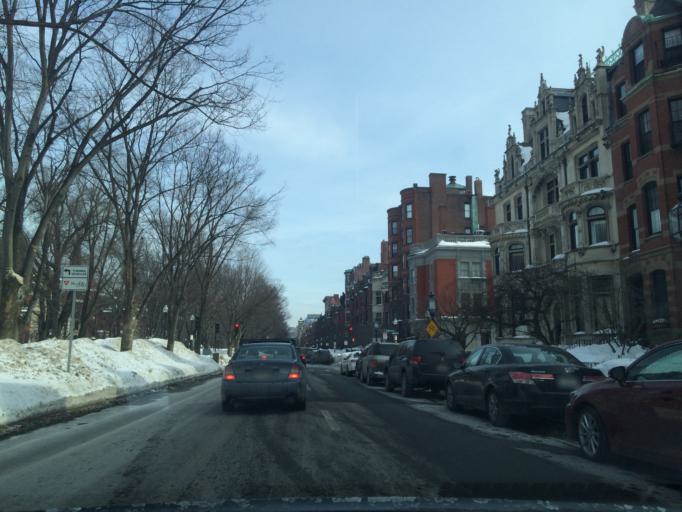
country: US
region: Massachusetts
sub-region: Suffolk County
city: Boston
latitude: 42.3494
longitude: -71.0867
